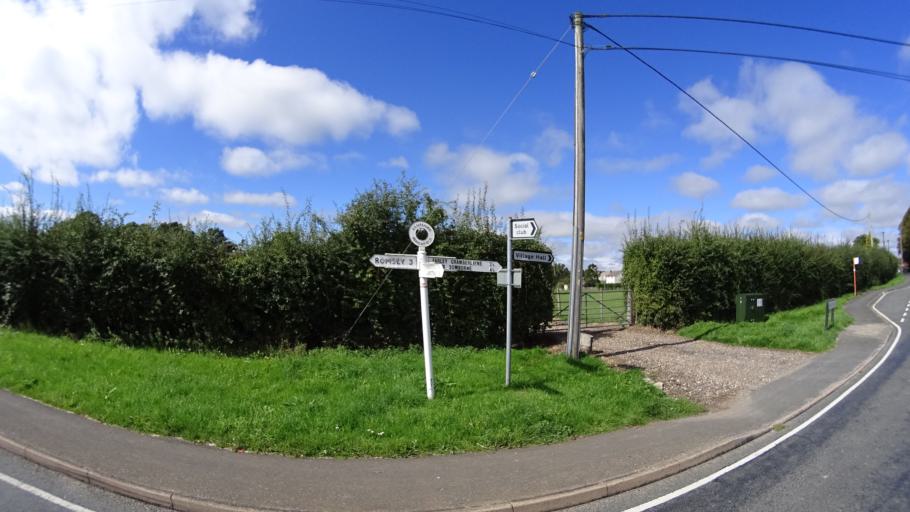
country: GB
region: England
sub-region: Hampshire
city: Romsey
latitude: 51.0207
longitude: -1.4662
